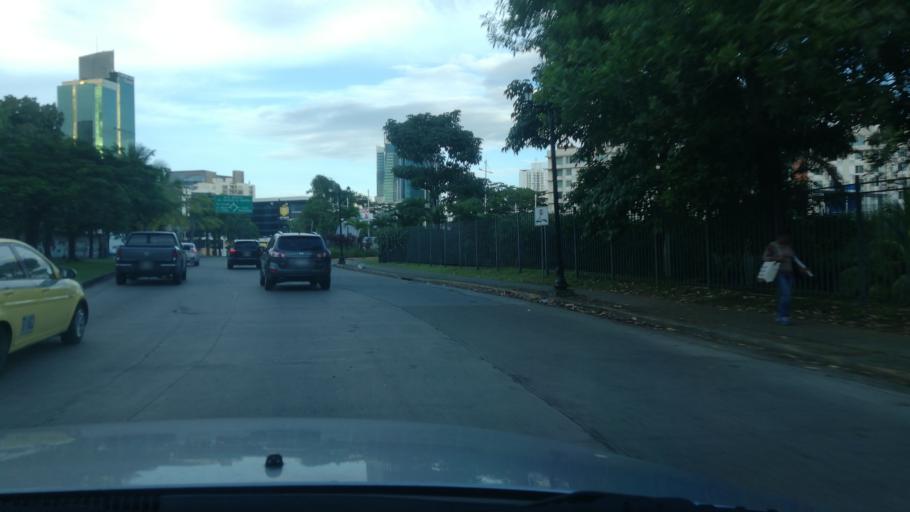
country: PA
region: Panama
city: Panama
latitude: 8.9832
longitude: -79.5113
